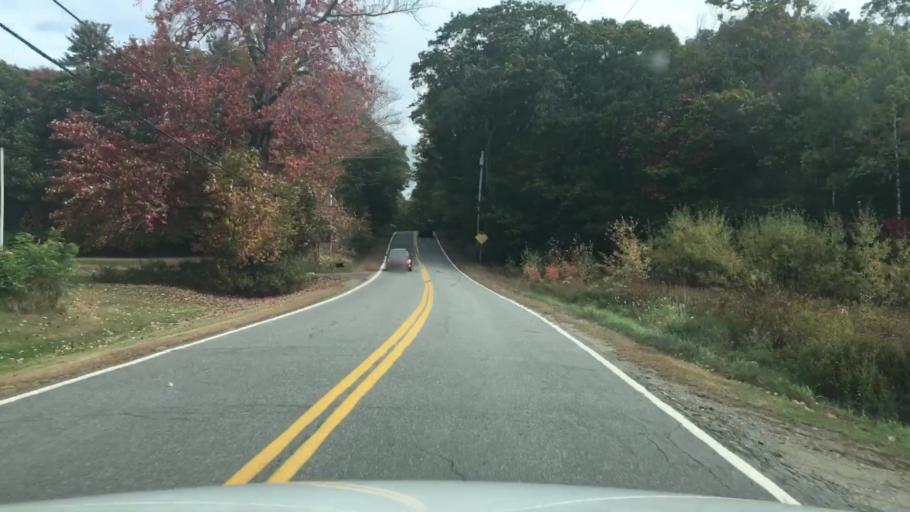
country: US
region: Maine
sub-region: Knox County
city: Hope
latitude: 44.2895
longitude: -69.1179
